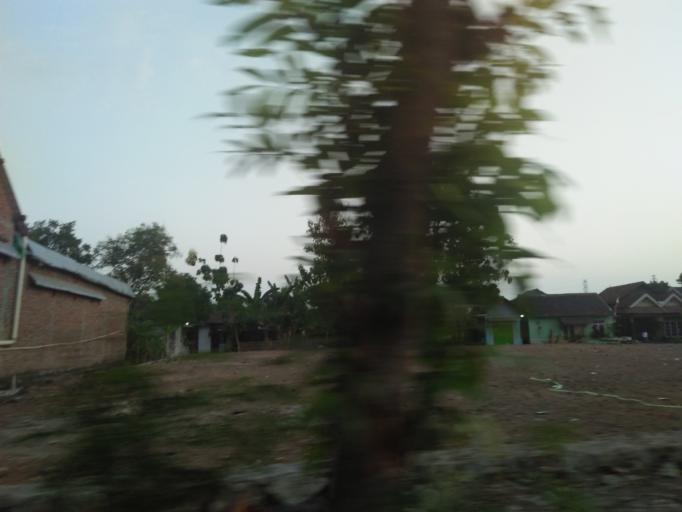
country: ID
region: Daerah Istimewa Yogyakarta
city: Sewon
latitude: -7.8435
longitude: 110.3927
